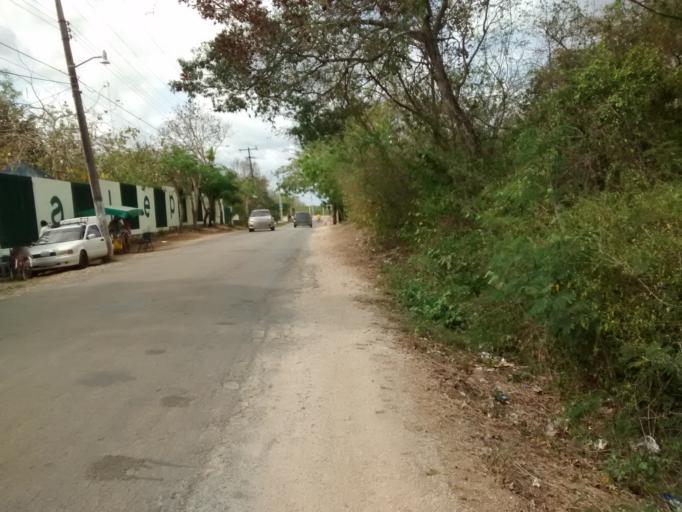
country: MX
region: Yucatan
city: Valladolid
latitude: 20.6896
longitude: -88.1811
